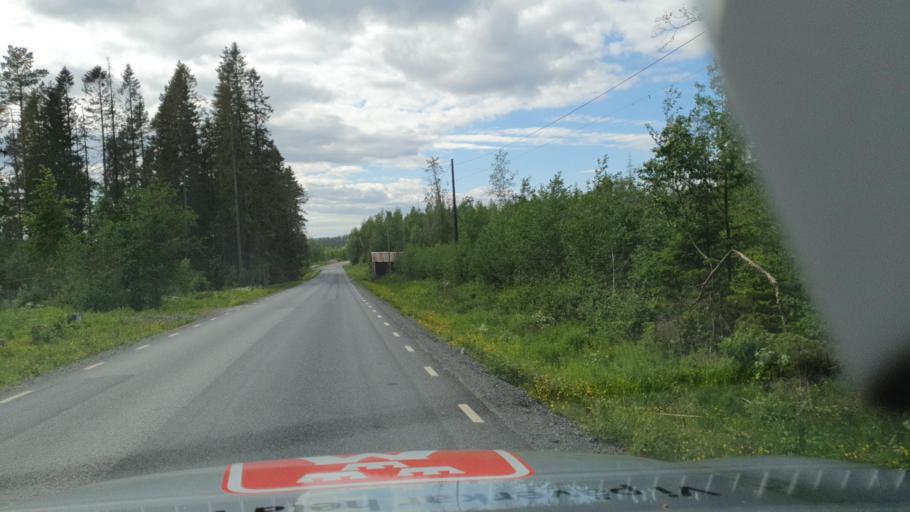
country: SE
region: Vaesternorrland
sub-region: Haernoesands Kommun
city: Haernoesand
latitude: 62.8089
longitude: 17.9929
